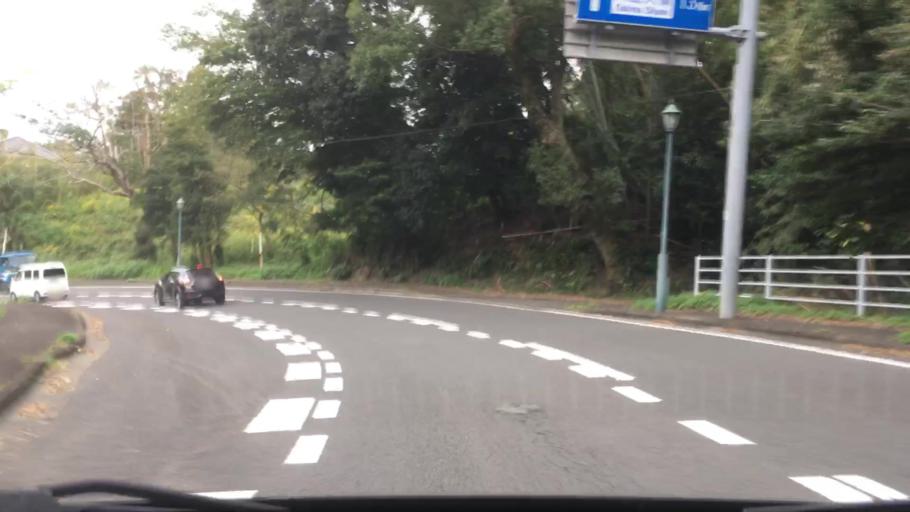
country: JP
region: Nagasaki
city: Sasebo
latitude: 33.0362
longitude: 129.6629
